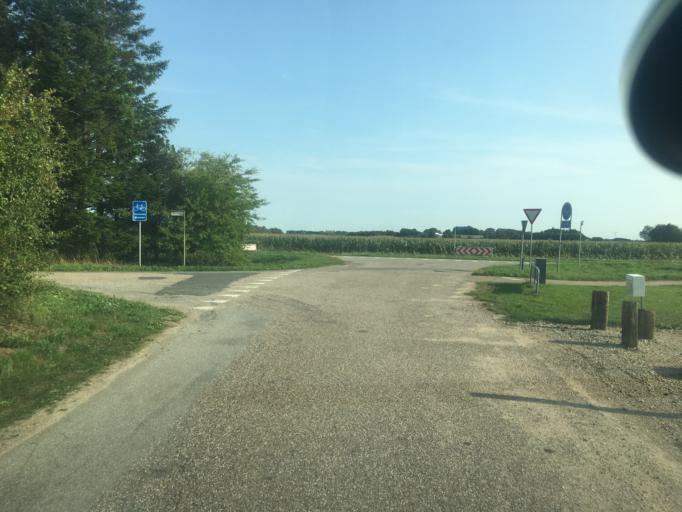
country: DK
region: South Denmark
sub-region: Tonder Kommune
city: Tonder
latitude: 54.9549
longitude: 8.8998
